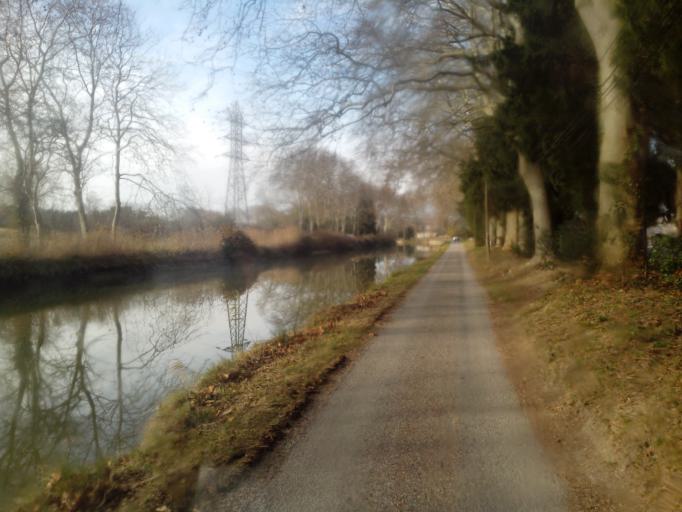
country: FR
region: Languedoc-Roussillon
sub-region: Departement de l'Aude
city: Castelnaudary
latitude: 43.3085
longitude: 1.9690
